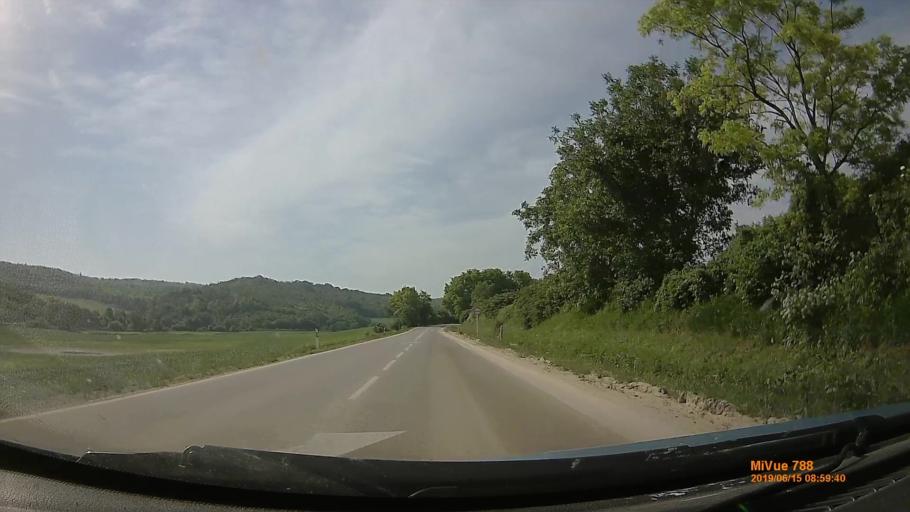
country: HU
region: Somogy
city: Adand
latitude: 46.7865
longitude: 18.1491
